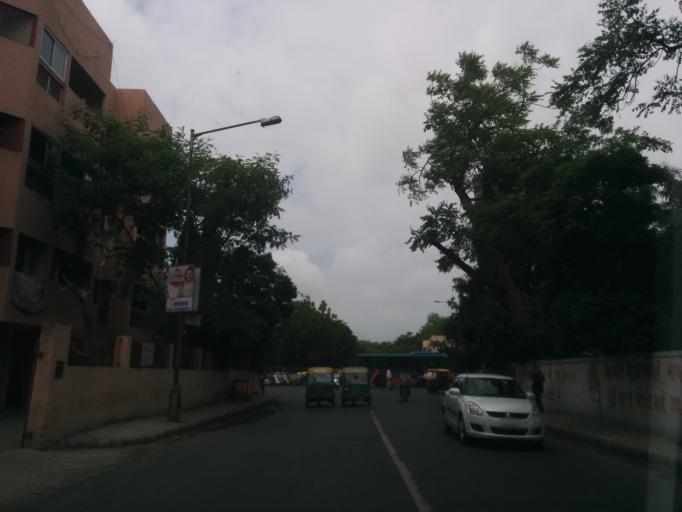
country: IN
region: Gujarat
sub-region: Ahmadabad
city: Ahmedabad
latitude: 23.0330
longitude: 72.5500
